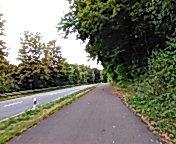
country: DE
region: Rheinland-Pfalz
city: Oberbillig
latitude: 49.7508
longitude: 6.4998
